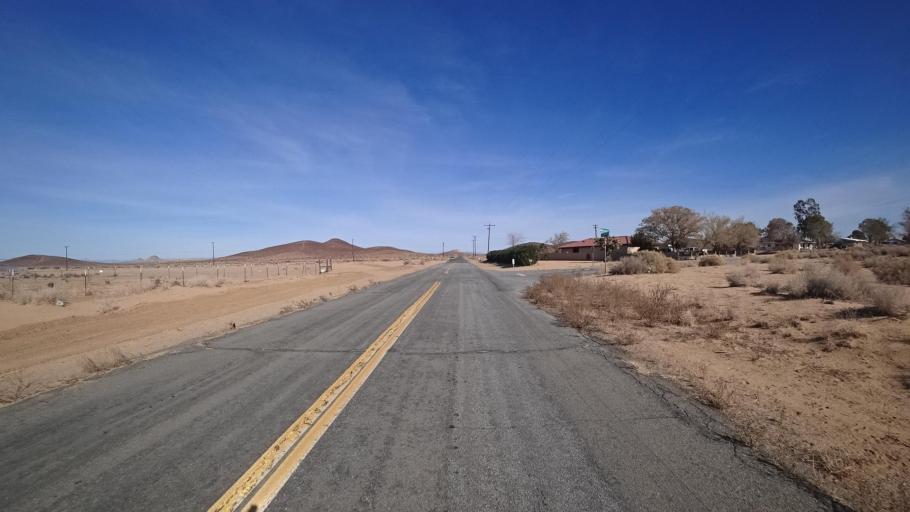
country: US
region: California
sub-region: Kern County
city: North Edwards
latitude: 35.0269
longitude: -117.8313
